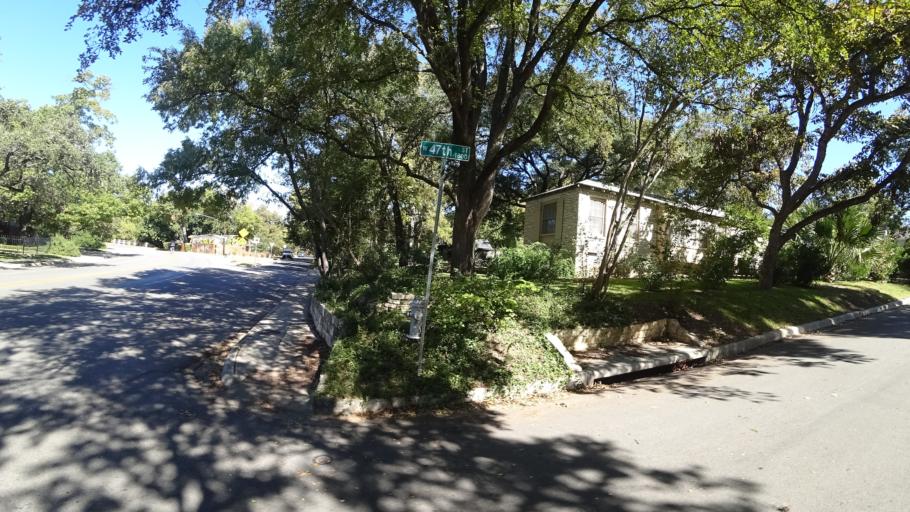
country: US
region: Texas
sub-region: Travis County
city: Austin
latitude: 30.3202
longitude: -97.7443
